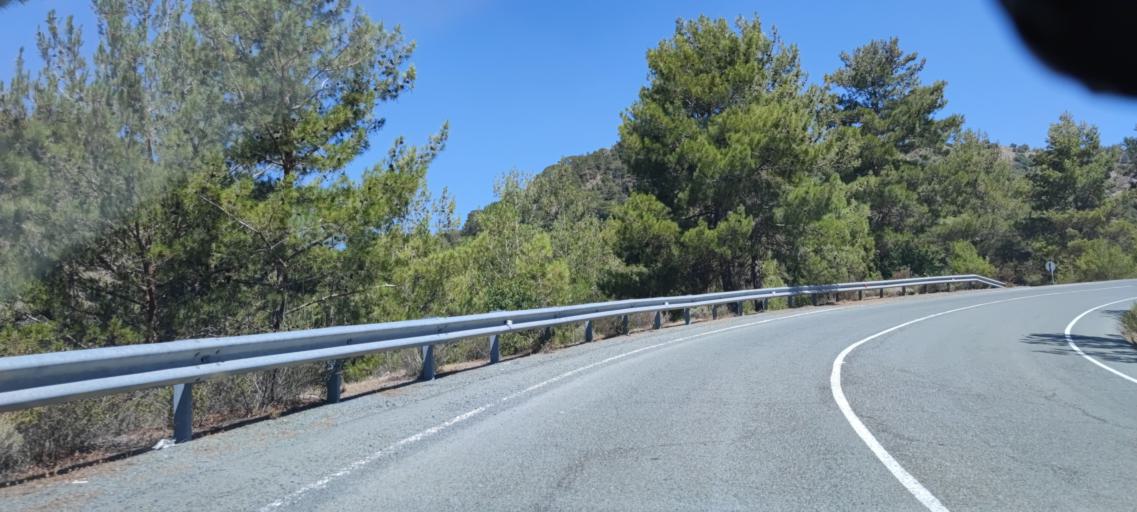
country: CY
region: Lefkosia
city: Kakopetria
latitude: 34.9067
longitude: 32.8124
